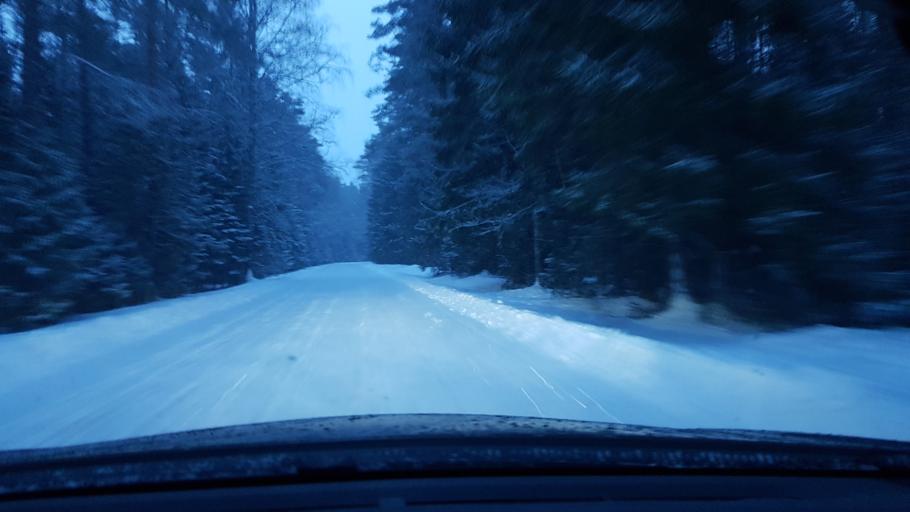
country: EE
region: Harju
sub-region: Kuusalu vald
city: Kuusalu
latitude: 59.5073
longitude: 25.5777
